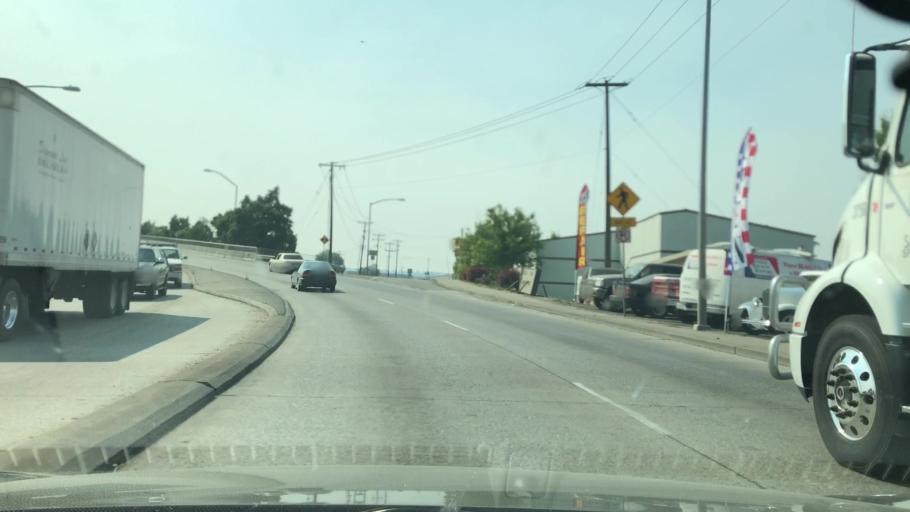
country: US
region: Washington
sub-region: Spokane County
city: Spokane
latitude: 47.6713
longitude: -117.3638
